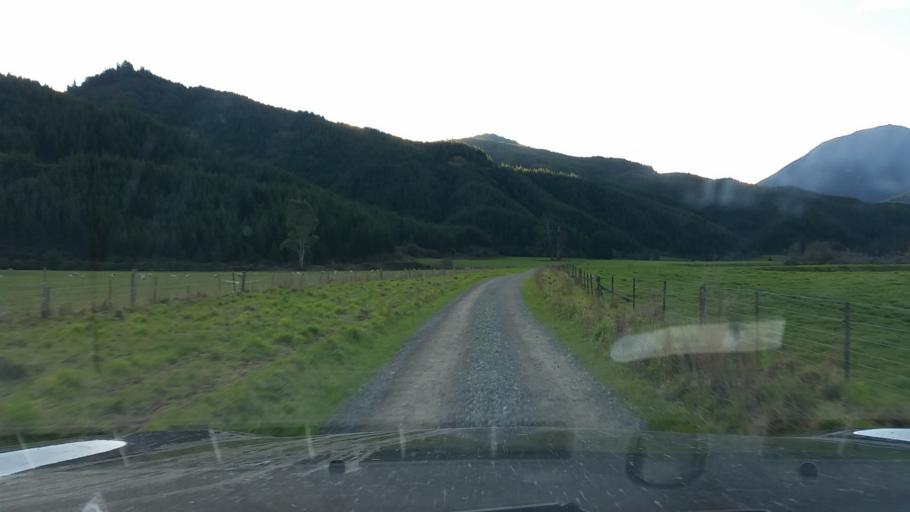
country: NZ
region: Nelson
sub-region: Nelson City
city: Nelson
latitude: -41.5358
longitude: 173.4898
